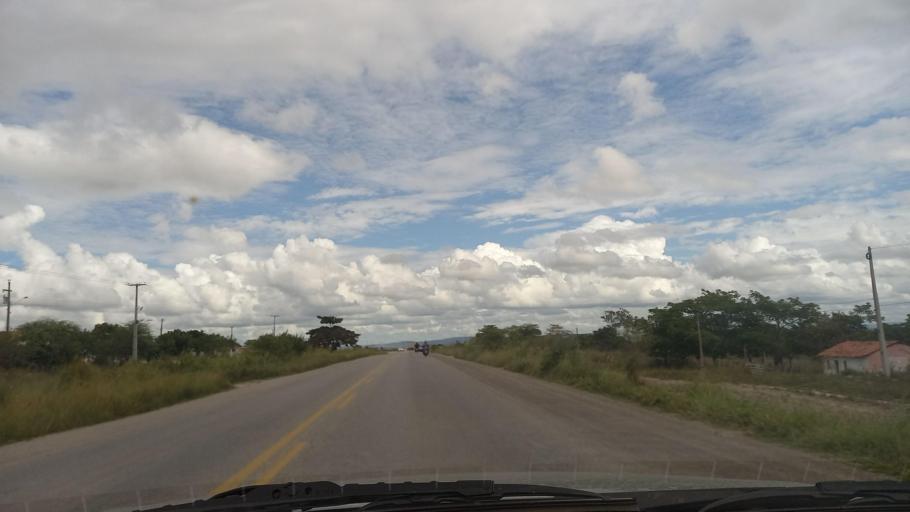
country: BR
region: Pernambuco
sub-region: Cachoeirinha
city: Cachoeirinha
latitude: -8.3723
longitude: -36.1727
